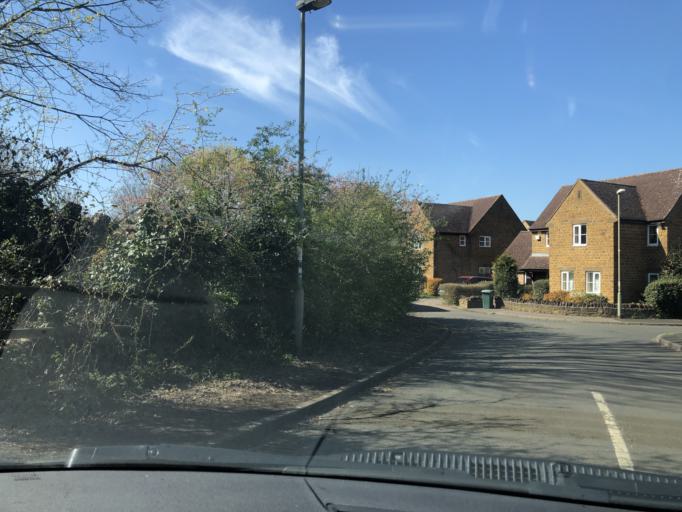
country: GB
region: England
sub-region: Oxfordshire
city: Hook Norton
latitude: 51.9993
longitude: -1.4752
